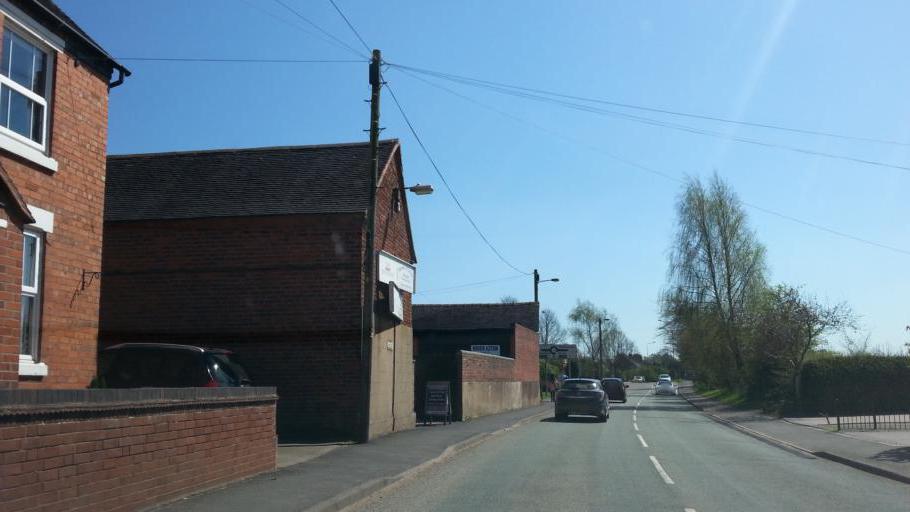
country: GB
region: England
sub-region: Staffordshire
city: Featherstone
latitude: 52.6559
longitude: -2.1316
